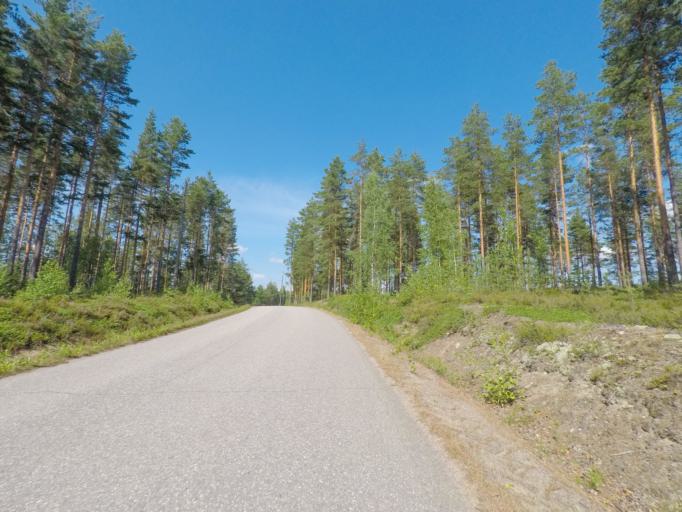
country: FI
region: Southern Savonia
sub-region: Mikkeli
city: Puumala
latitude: 61.4313
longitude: 28.1703
